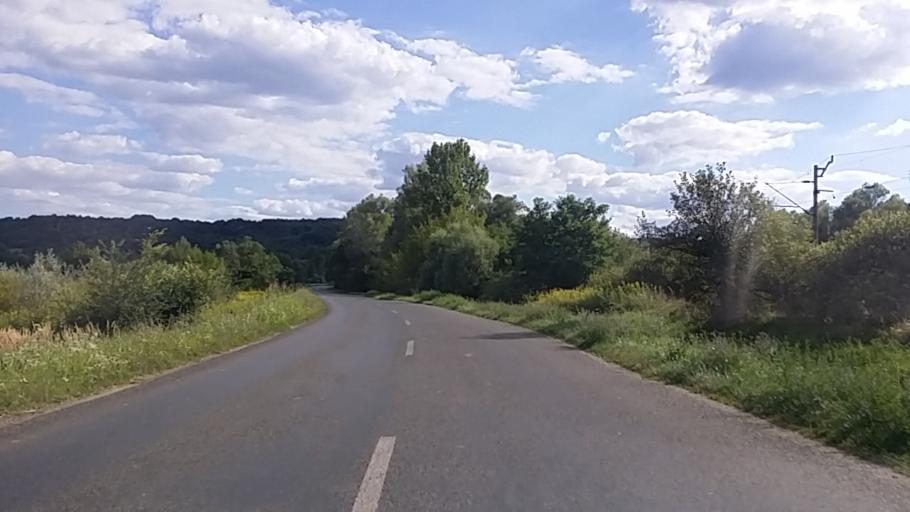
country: HU
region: Baranya
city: Sasd
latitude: 46.2141
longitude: 18.1045
